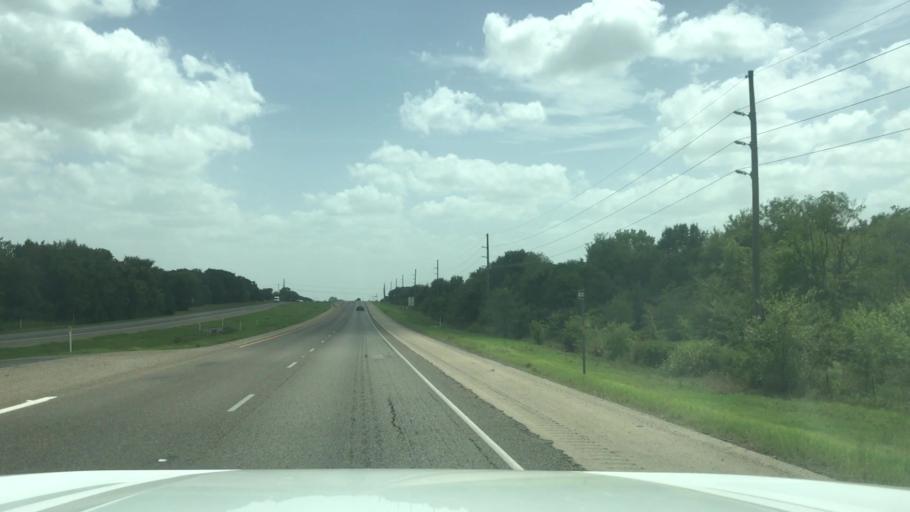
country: US
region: Texas
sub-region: Robertson County
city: Calvert
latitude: 31.1093
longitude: -96.7134
